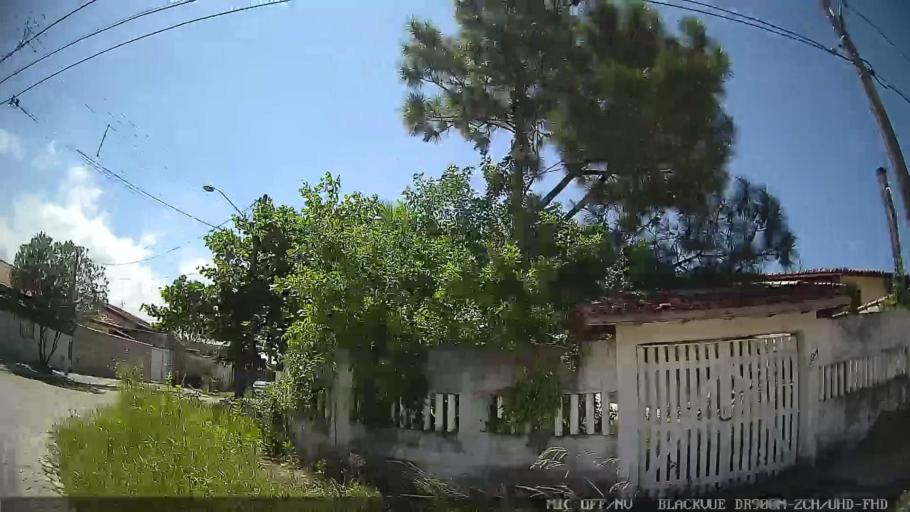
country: BR
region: Sao Paulo
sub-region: Peruibe
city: Peruibe
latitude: -24.3025
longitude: -46.9926
